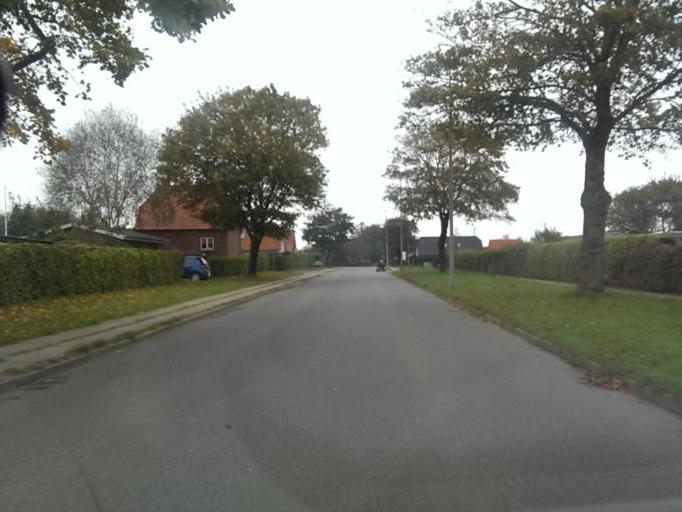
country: DK
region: South Denmark
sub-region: Esbjerg Kommune
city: Bramming
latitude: 55.4679
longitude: 8.7118
